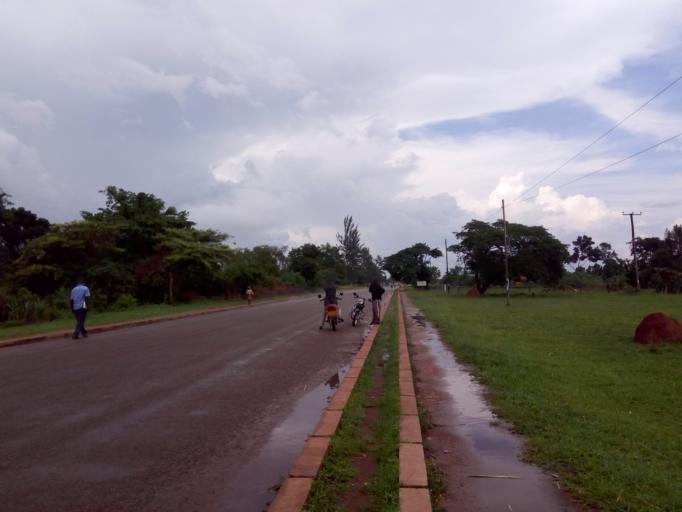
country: UG
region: Western Region
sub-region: Masindi District
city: Masindi
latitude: 1.6877
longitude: 31.7062
